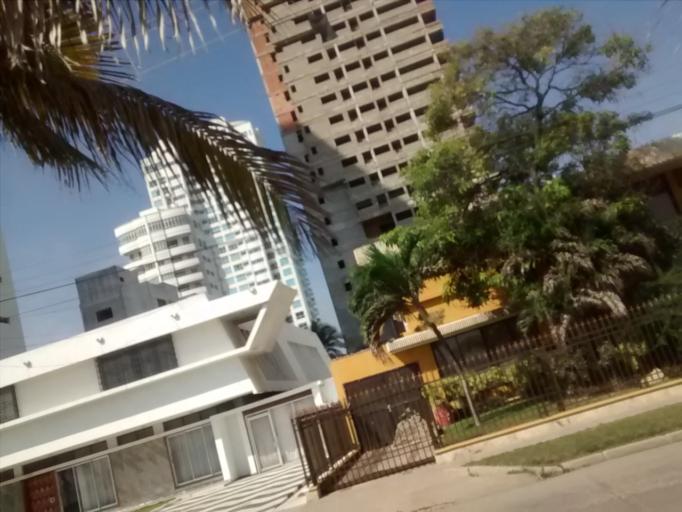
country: CO
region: Bolivar
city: Cartagena
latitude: 10.3960
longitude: -75.5518
